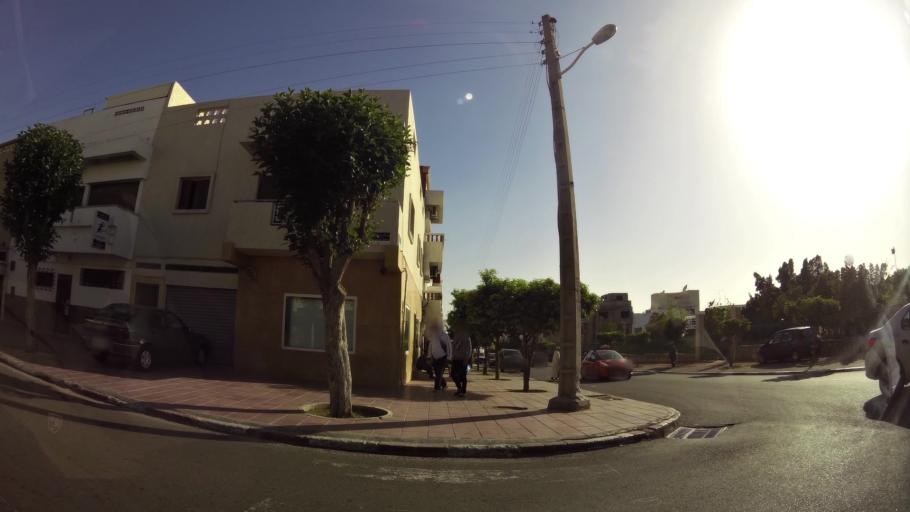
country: MA
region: Souss-Massa-Draa
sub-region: Agadir-Ida-ou-Tnan
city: Agadir
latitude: 30.4320
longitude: -9.5796
